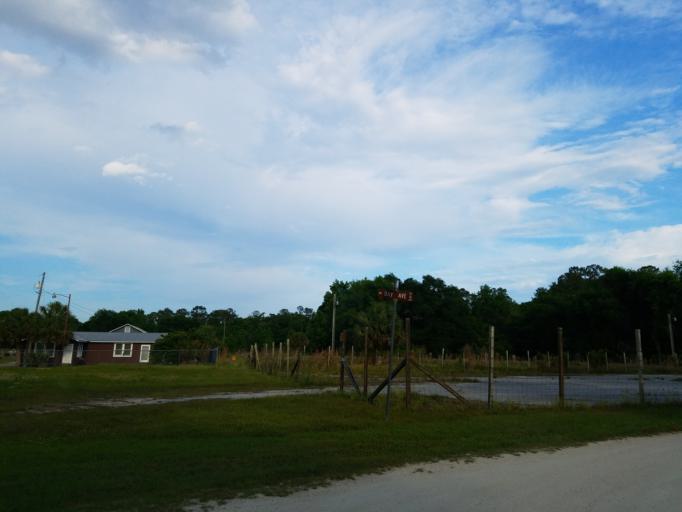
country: US
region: Florida
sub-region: Alachua County
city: Gainesville
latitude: 29.5073
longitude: -82.2753
